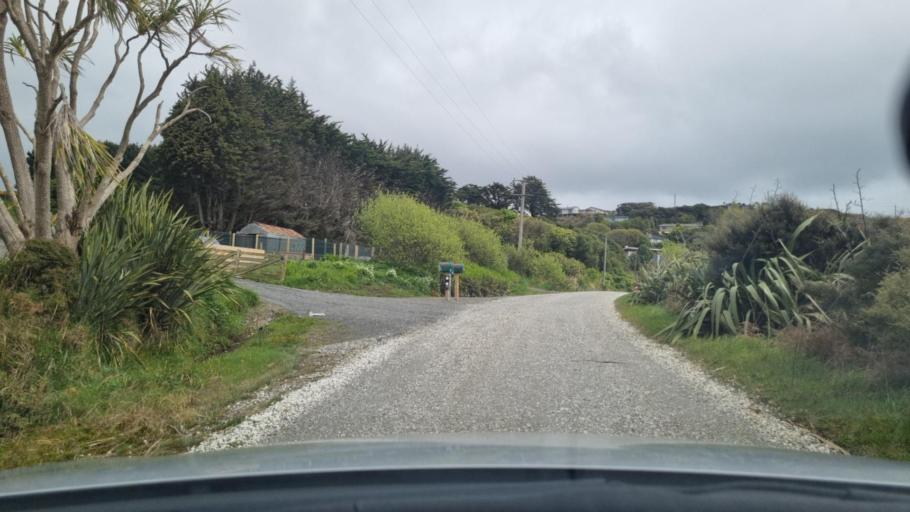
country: NZ
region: Southland
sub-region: Invercargill City
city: Bluff
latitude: -46.5763
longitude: 168.3018
